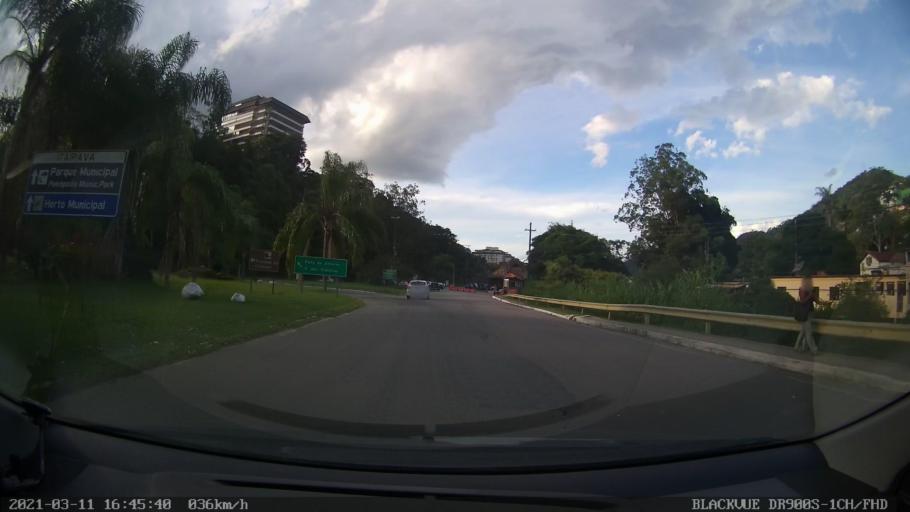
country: BR
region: Rio de Janeiro
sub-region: Petropolis
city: Petropolis
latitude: -22.4138
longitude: -43.1399
